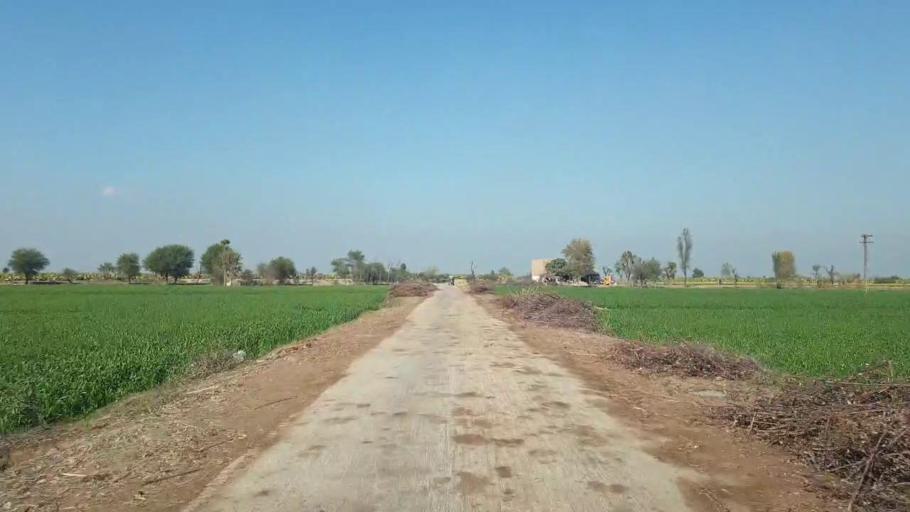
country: PK
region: Sindh
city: Shahdadpur
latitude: 25.9125
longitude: 68.5529
